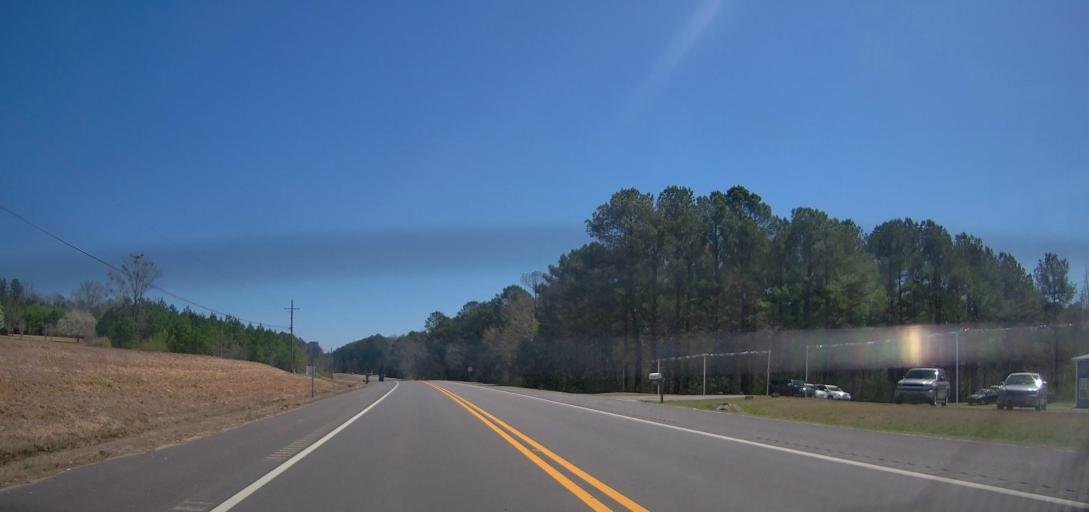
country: US
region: Alabama
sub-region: Calhoun County
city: Ohatchee
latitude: 33.7832
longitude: -86.0340
